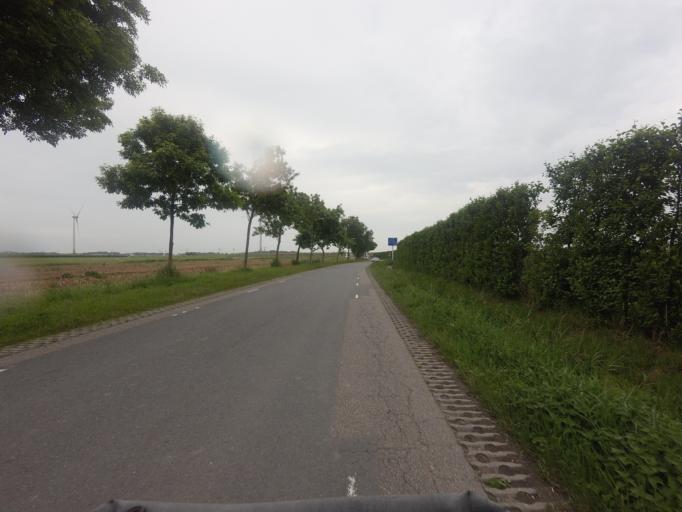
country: NL
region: North Holland
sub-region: Gemeente Hoorn
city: Hoorn
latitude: 52.6891
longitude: 5.1265
